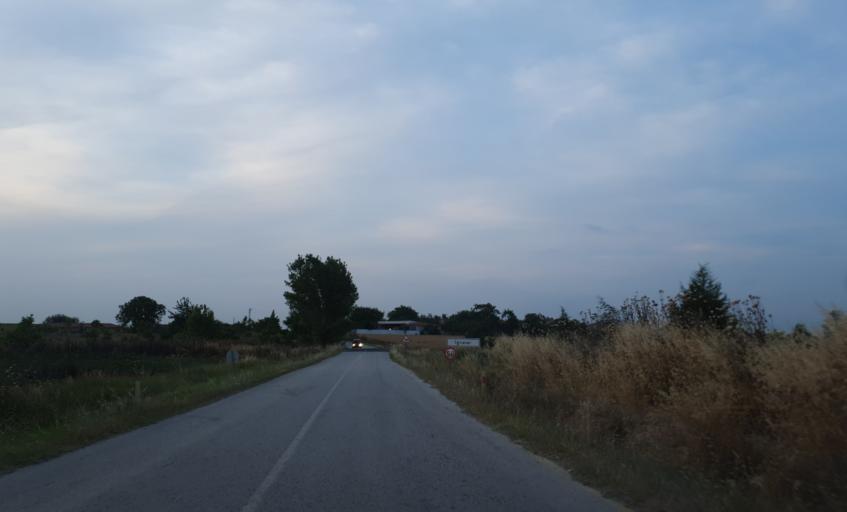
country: TR
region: Kirklareli
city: Buyukkaristiran
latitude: 41.3411
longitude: 27.6048
